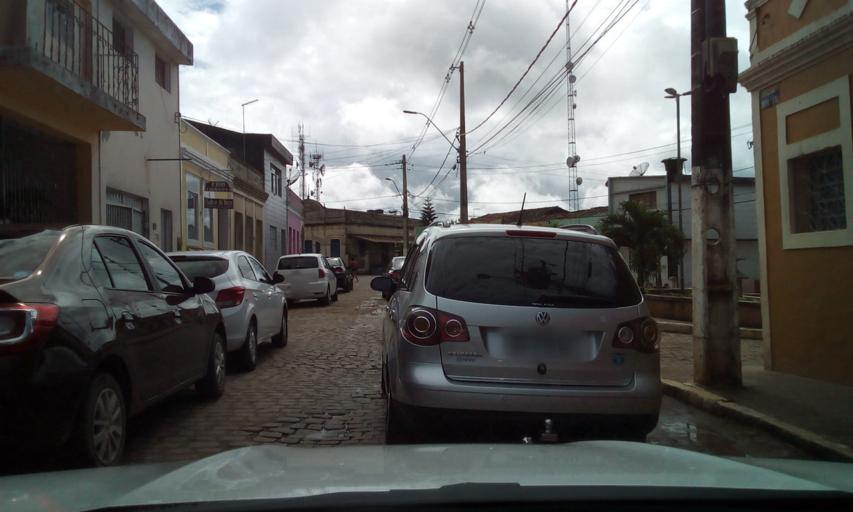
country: BR
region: Paraiba
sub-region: Areia
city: Areia
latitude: -6.9681
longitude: -35.7006
